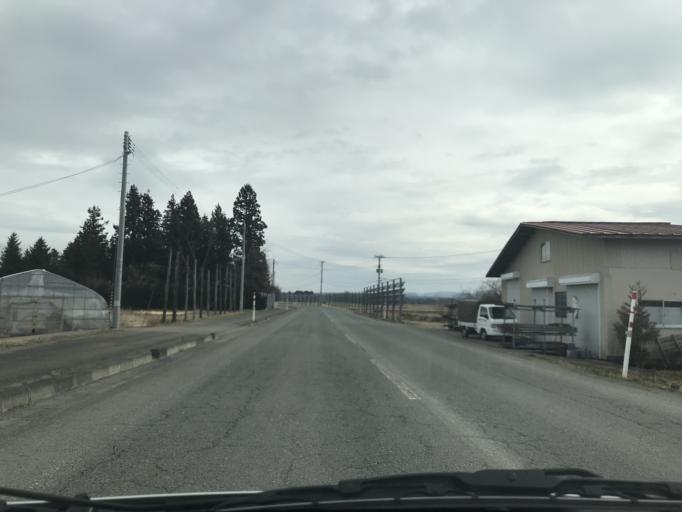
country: JP
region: Iwate
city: Kitakami
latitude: 39.3309
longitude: 140.9955
